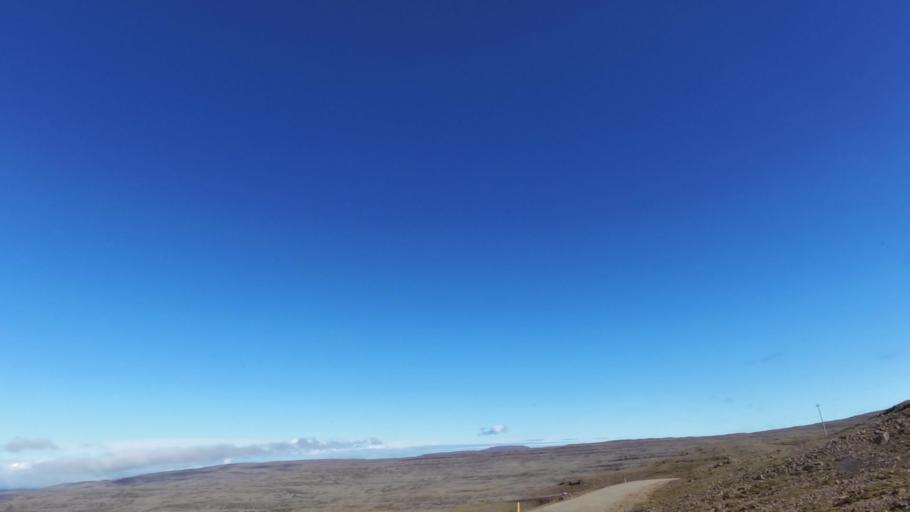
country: IS
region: West
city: Olafsvik
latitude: 65.5559
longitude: -24.2303
